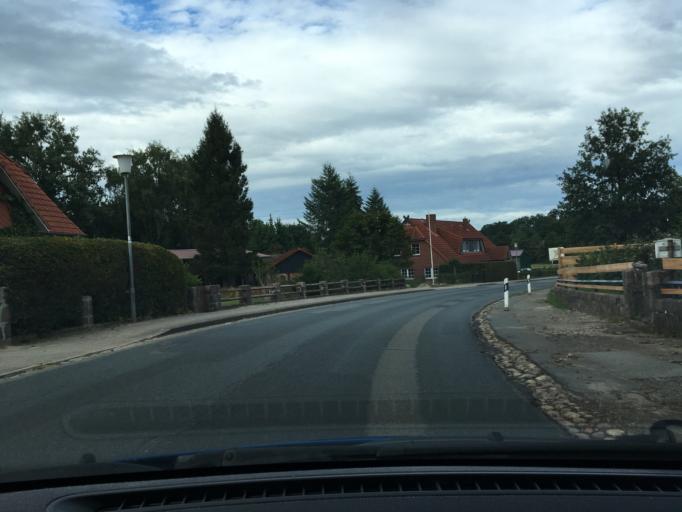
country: DE
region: Lower Saxony
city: Egestorf
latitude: 53.2008
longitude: 10.0225
